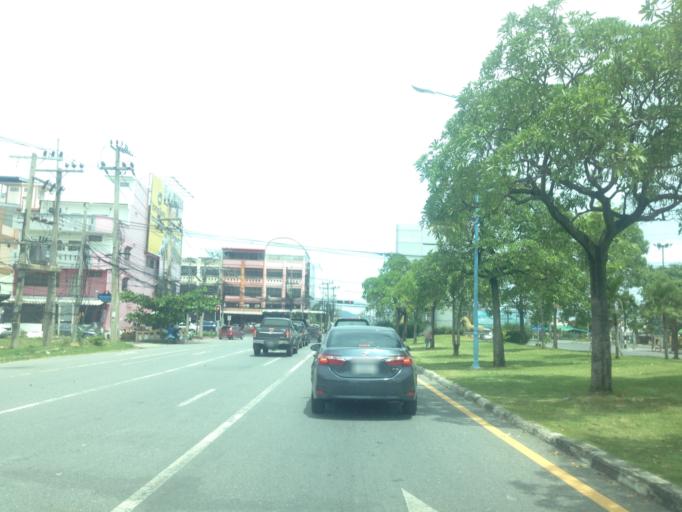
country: TH
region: Chon Buri
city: Chon Buri
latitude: 13.3387
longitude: 100.9506
